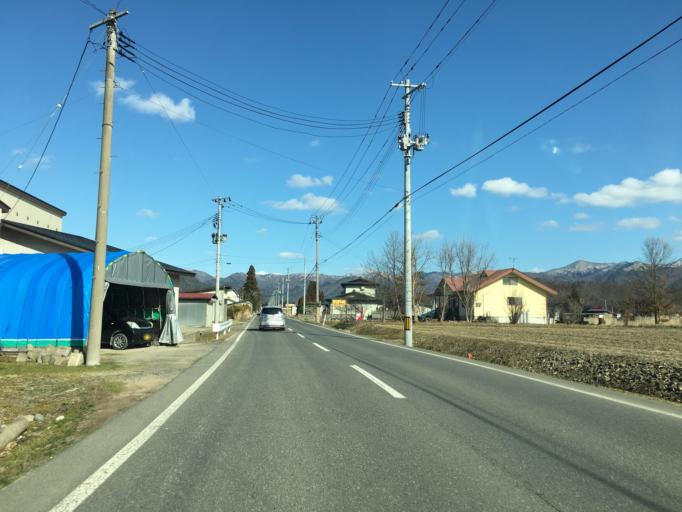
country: JP
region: Yamagata
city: Takahata
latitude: 37.9531
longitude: 140.1669
